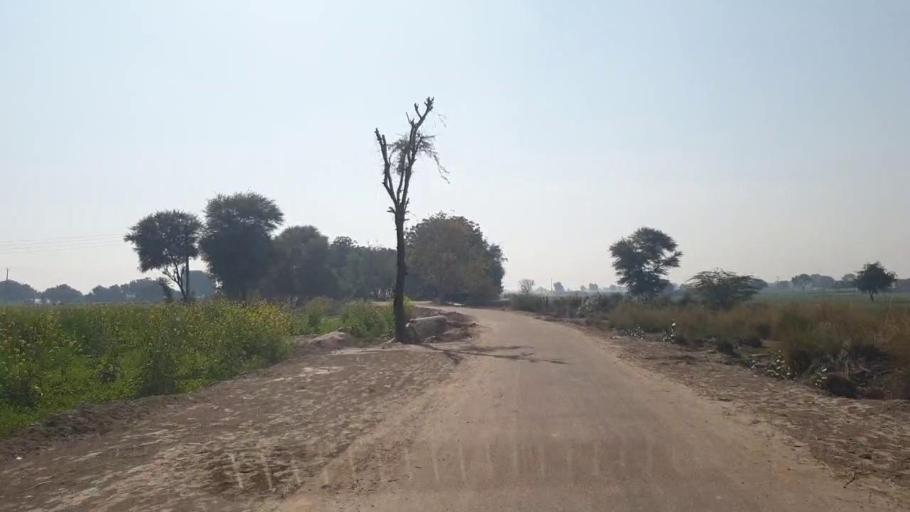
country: PK
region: Sindh
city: Shahpur Chakar
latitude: 26.1091
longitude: 68.6007
